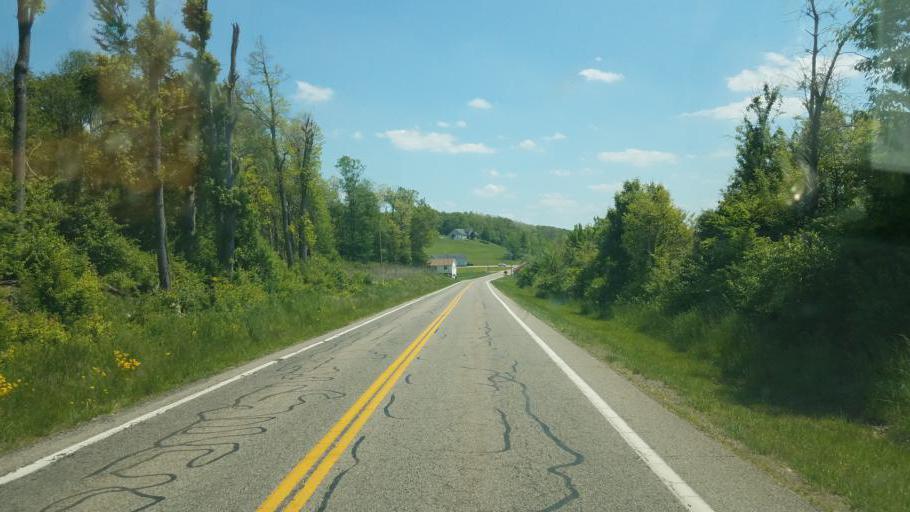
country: US
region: Ohio
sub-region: Muskingum County
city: Frazeysburg
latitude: 40.1705
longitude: -82.2246
